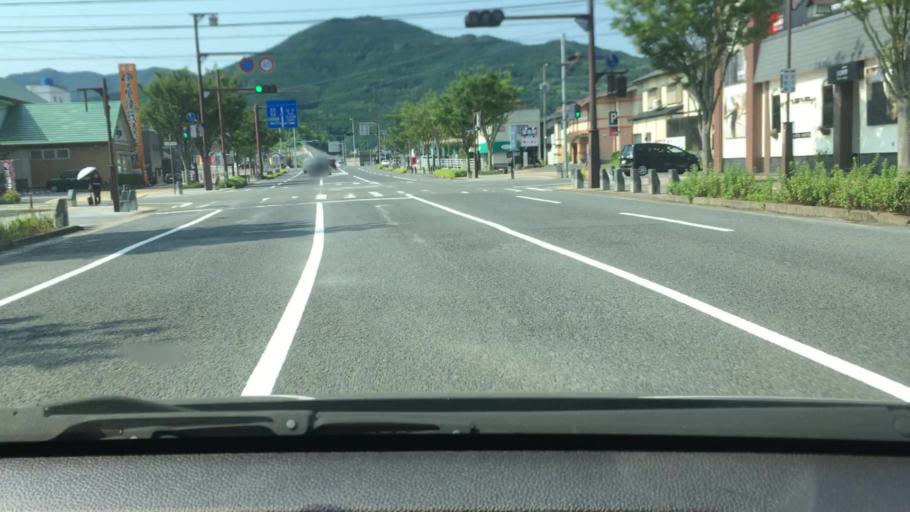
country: JP
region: Saga Prefecture
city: Imaricho-ko
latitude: 33.2707
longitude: 129.8761
